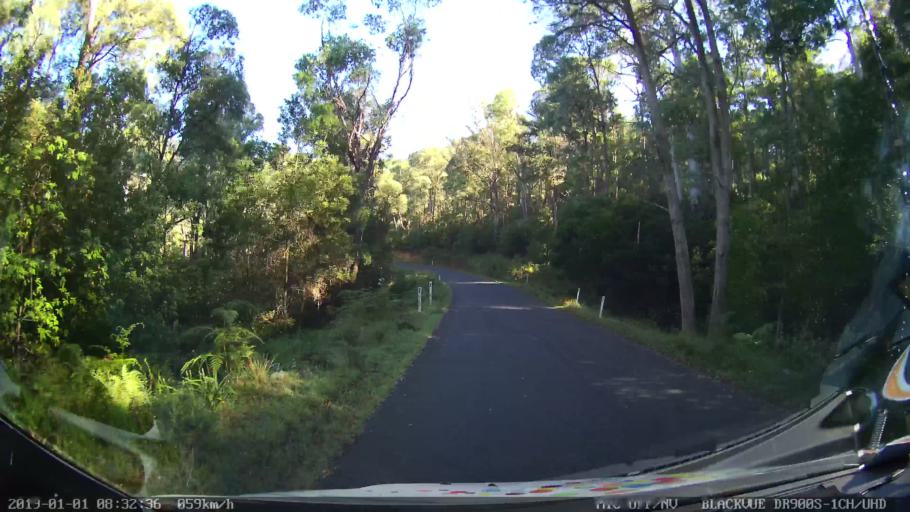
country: AU
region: New South Wales
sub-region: Snowy River
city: Jindabyne
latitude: -36.3604
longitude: 148.2063
